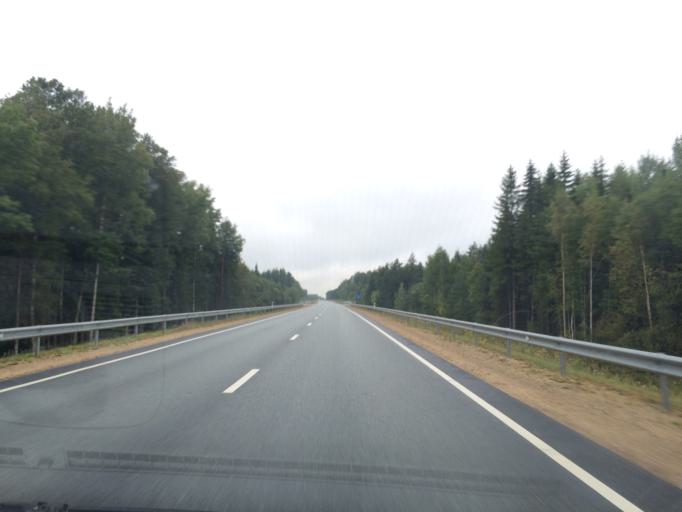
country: LV
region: Ogre
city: Jumprava
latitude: 56.8011
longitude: 24.9344
